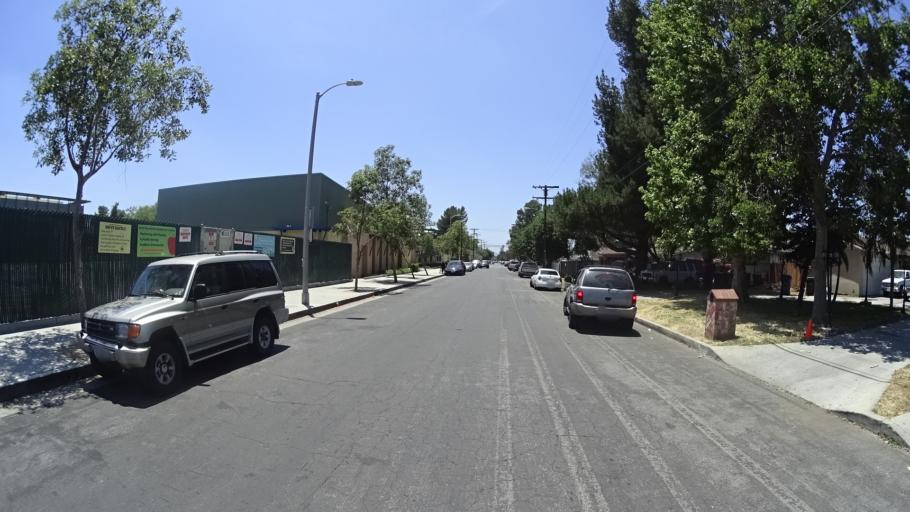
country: US
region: California
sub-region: Los Angeles County
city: Van Nuys
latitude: 34.2330
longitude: -118.4575
